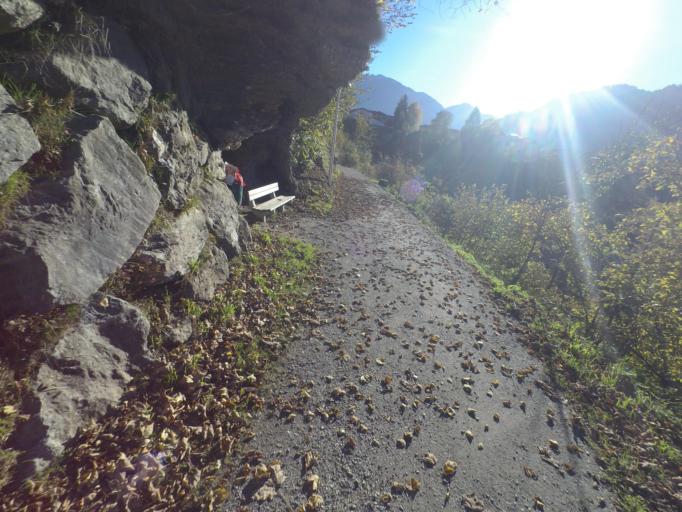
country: AT
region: Salzburg
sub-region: Politischer Bezirk Sankt Johann im Pongau
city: Sankt Johann im Pongau
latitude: 47.3517
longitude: 13.2046
